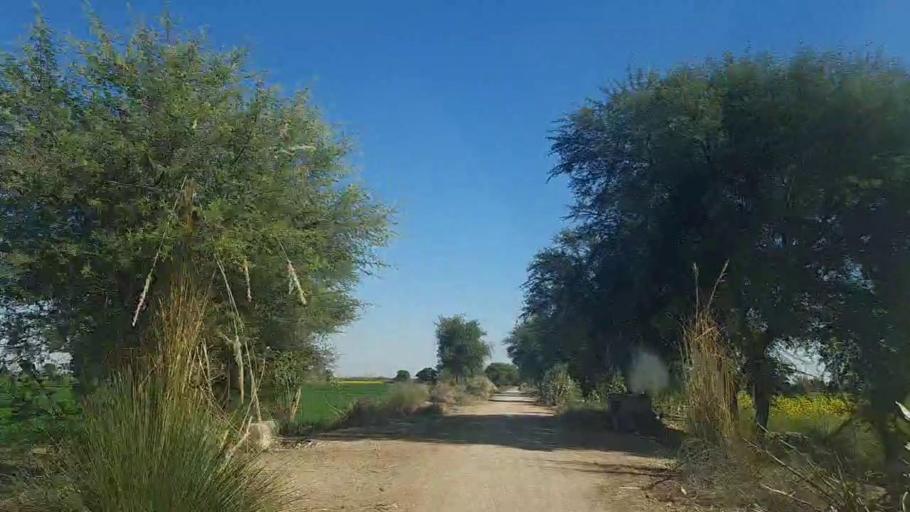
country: PK
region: Sindh
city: Khadro
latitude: 26.2180
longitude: 68.8655
